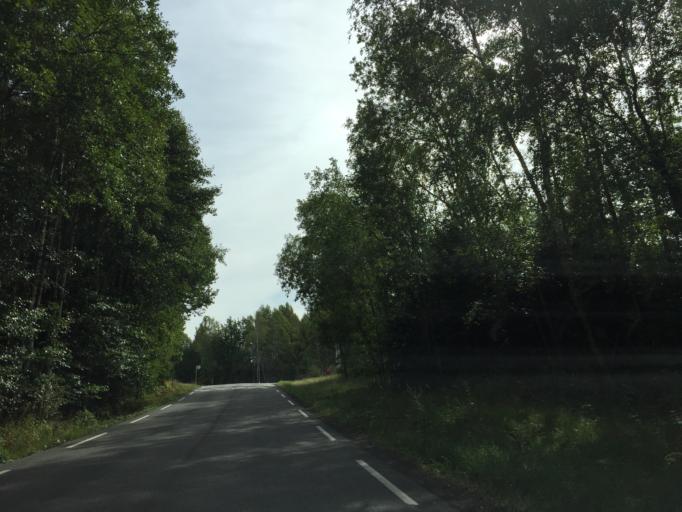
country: NO
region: Ostfold
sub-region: Moss
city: Moss
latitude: 59.4878
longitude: 10.6946
